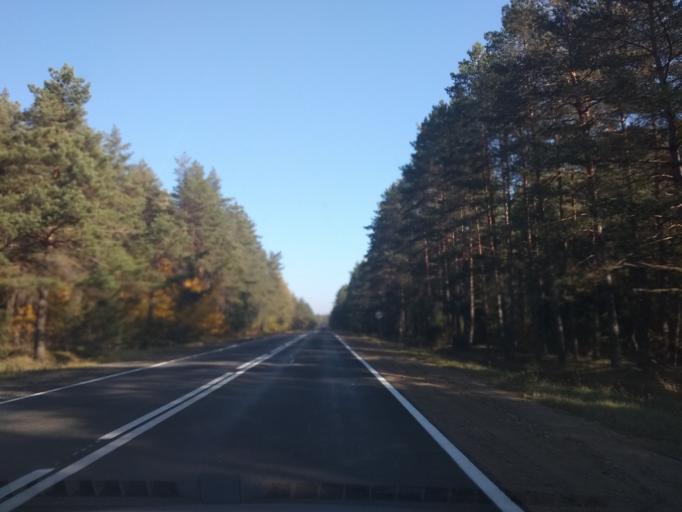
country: BY
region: Brest
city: Baranovichi
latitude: 53.0412
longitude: 25.8143
